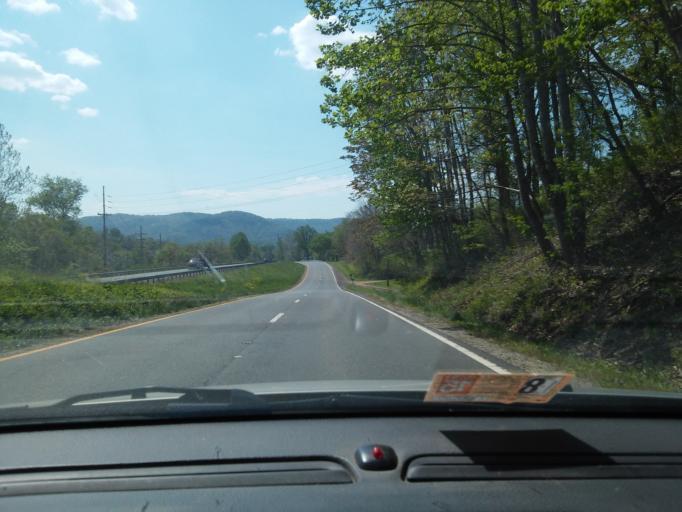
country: US
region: Virginia
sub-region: Rappahannock County
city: Washington
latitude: 38.7137
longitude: -78.1405
